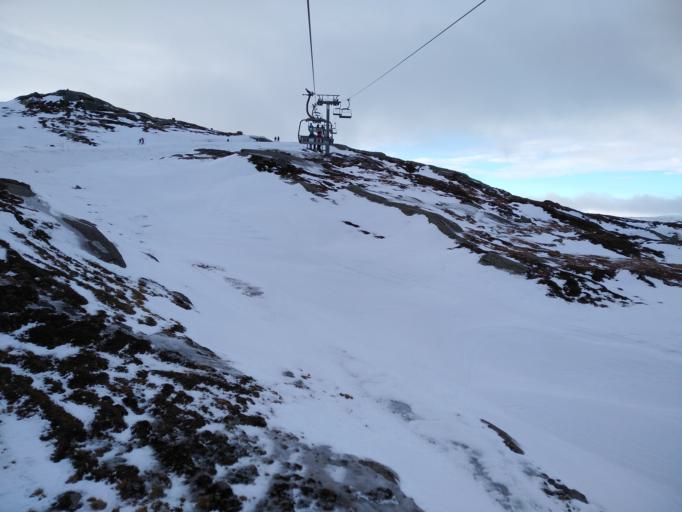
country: NO
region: Vest-Agder
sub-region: Sirdal
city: Tonstad
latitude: 58.9122
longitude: 6.8169
